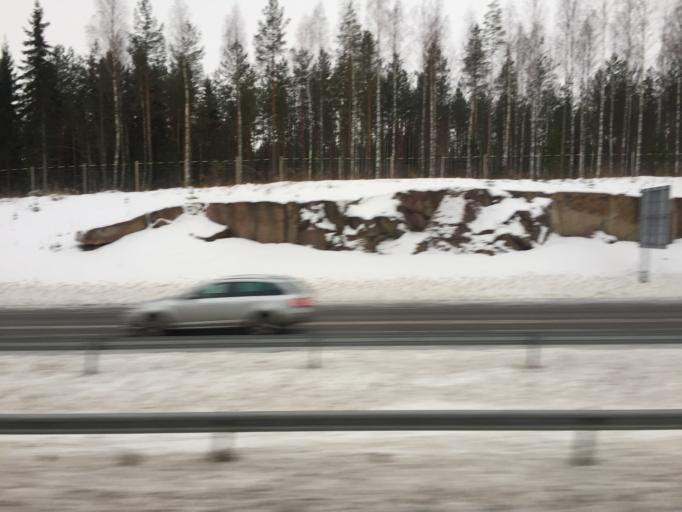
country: FI
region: Kymenlaakso
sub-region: Kotka-Hamina
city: Broby
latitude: 60.5017
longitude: 26.8088
